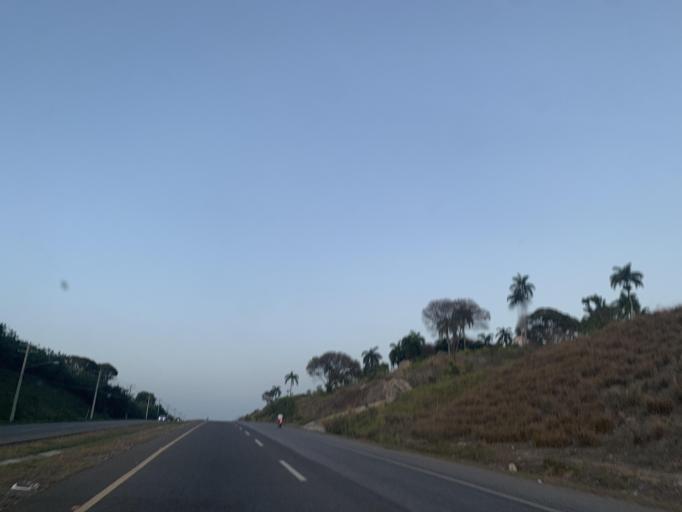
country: DO
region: Puerto Plata
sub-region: Puerto Plata
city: Puerto Plata
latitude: 19.8270
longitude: -70.7574
